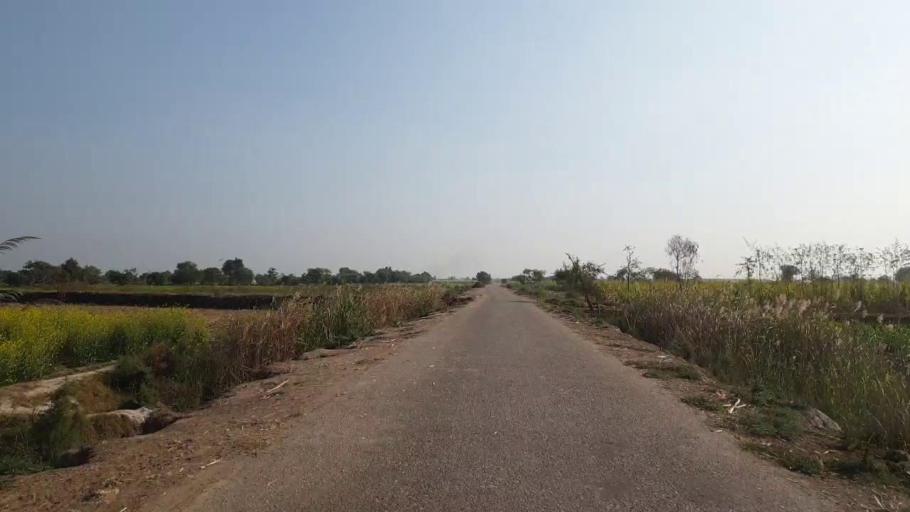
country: PK
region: Sindh
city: Tando Allahyar
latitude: 25.5899
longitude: 68.6207
